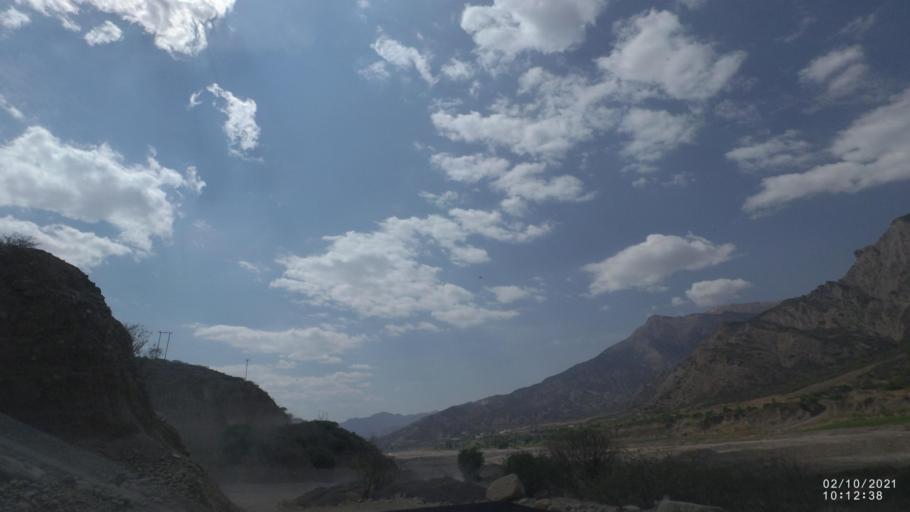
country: BO
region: Cochabamba
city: Irpa Irpa
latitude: -17.7319
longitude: -66.3226
